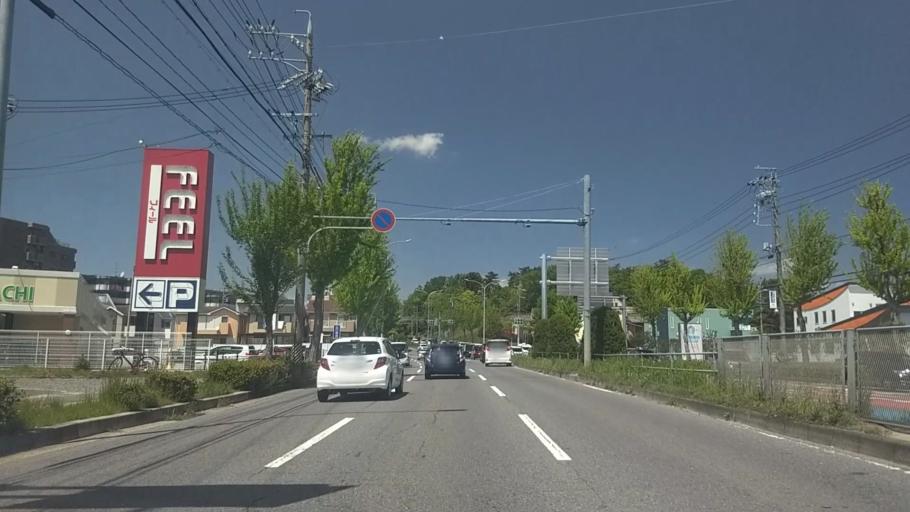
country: JP
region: Aichi
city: Okazaki
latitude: 34.9512
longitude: 137.1896
